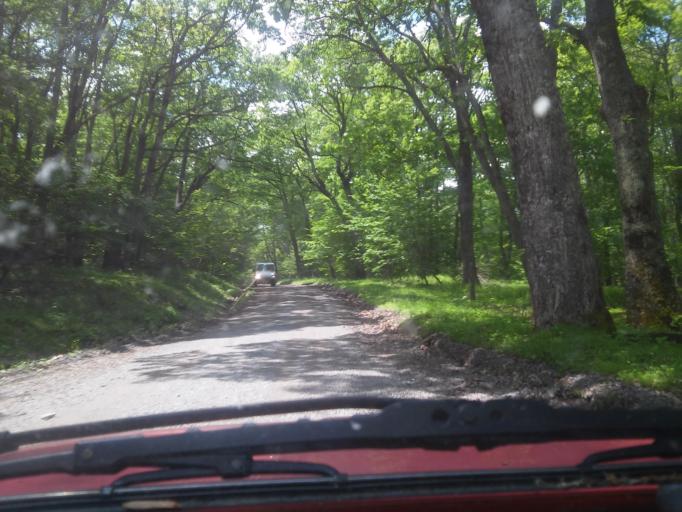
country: US
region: Virginia
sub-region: Giles County
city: Pembroke
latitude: 37.3726
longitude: -80.5259
